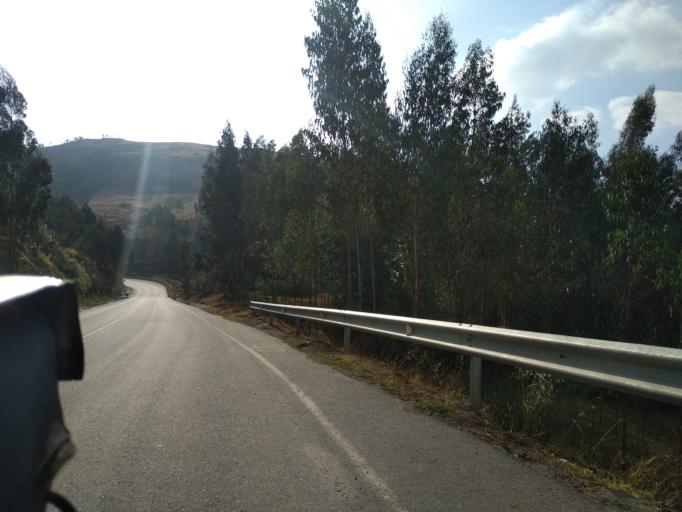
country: PE
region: La Libertad
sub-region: Provincia de Otuzco
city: Agallpampa
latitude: -7.9945
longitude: -78.5276
